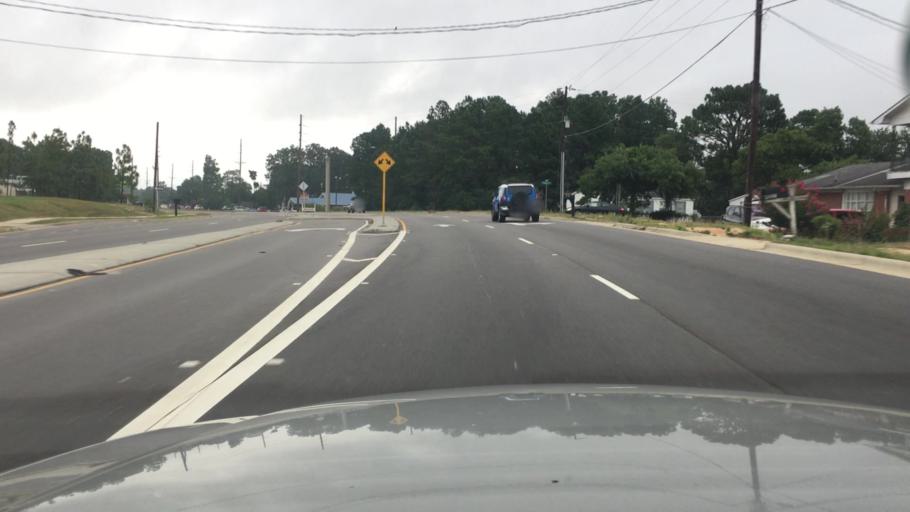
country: US
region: North Carolina
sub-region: Cumberland County
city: Hope Mills
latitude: 34.9863
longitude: -78.9268
